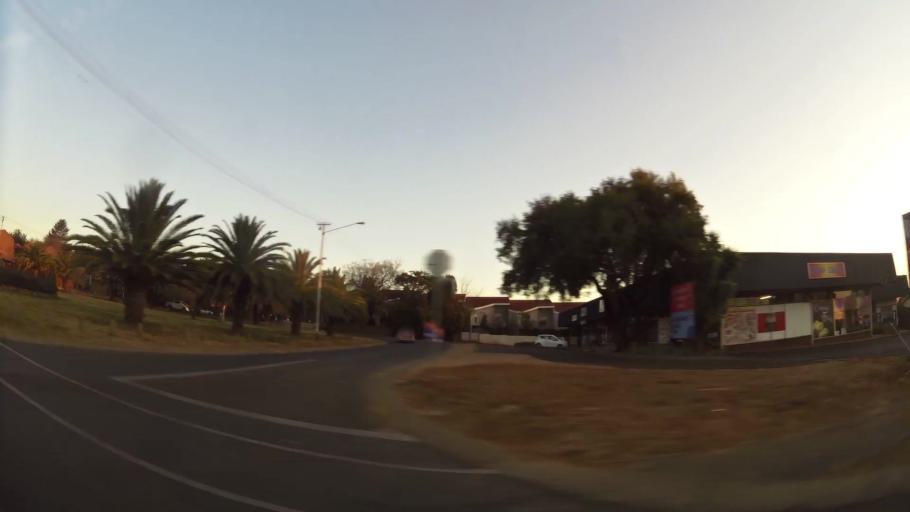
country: ZA
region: Gauteng
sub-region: City of Tshwane Metropolitan Municipality
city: Centurion
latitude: -25.8400
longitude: 28.1505
